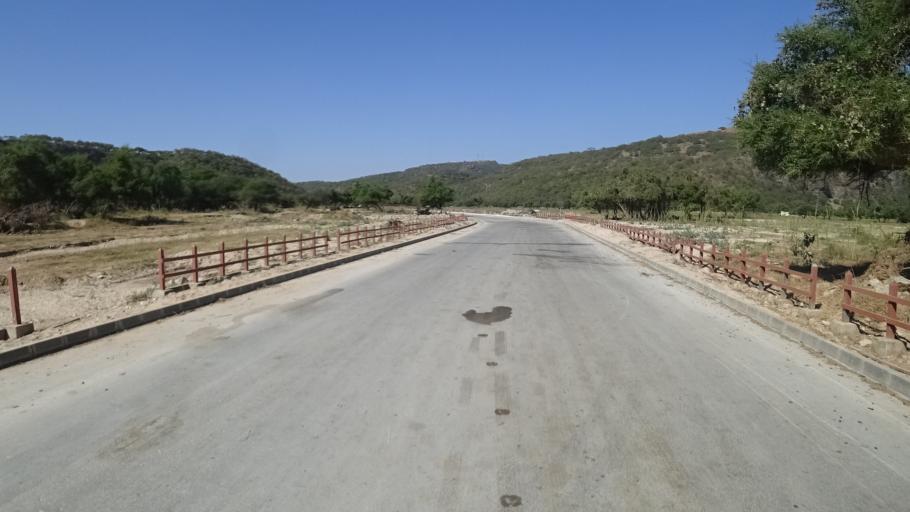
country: OM
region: Zufar
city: Salalah
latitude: 17.0898
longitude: 54.4358
